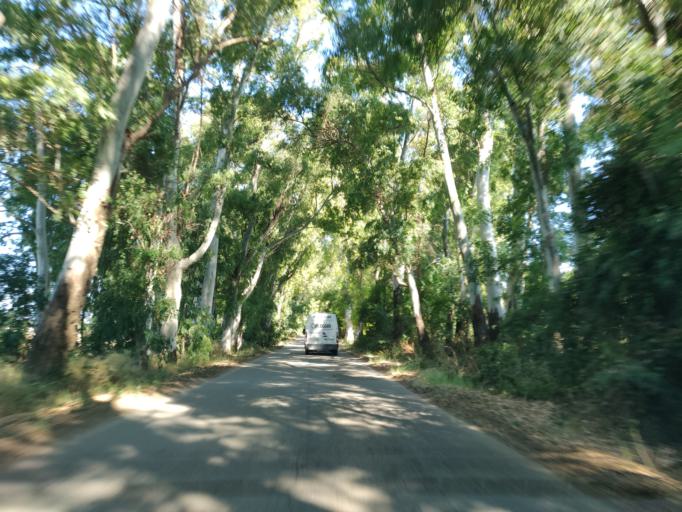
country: IT
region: Latium
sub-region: Citta metropolitana di Roma Capitale
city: Aurelia
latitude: 42.1623
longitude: 11.7459
